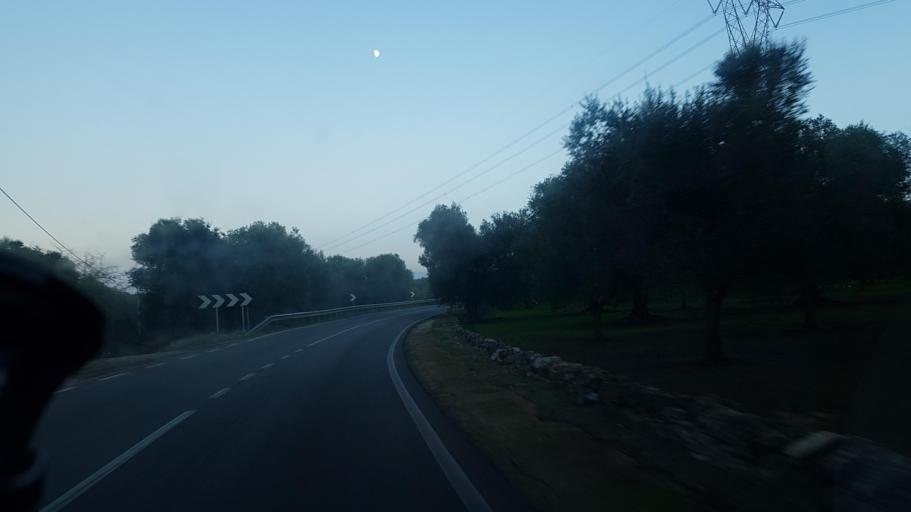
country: IT
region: Apulia
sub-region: Provincia di Brindisi
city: San Michele Salentino
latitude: 40.5906
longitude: 17.6604
